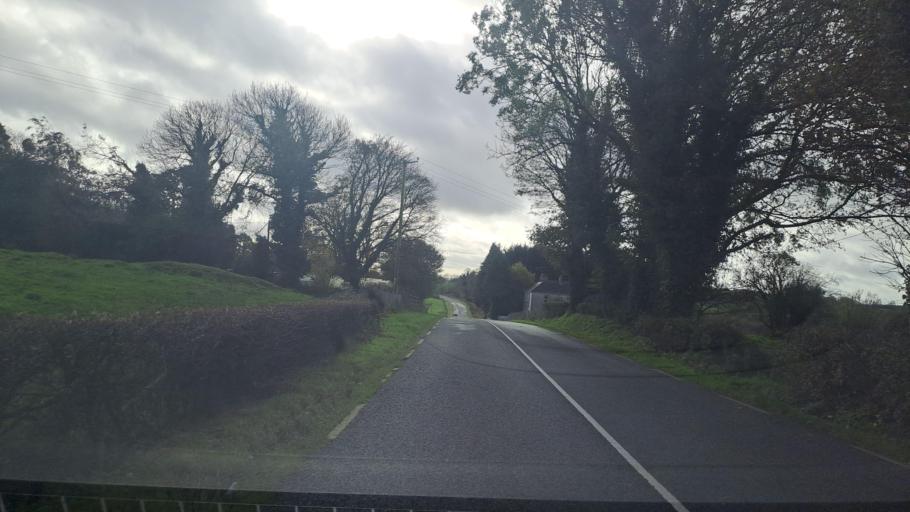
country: IE
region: Ulster
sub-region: County Monaghan
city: Monaghan
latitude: 54.1776
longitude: -6.9959
